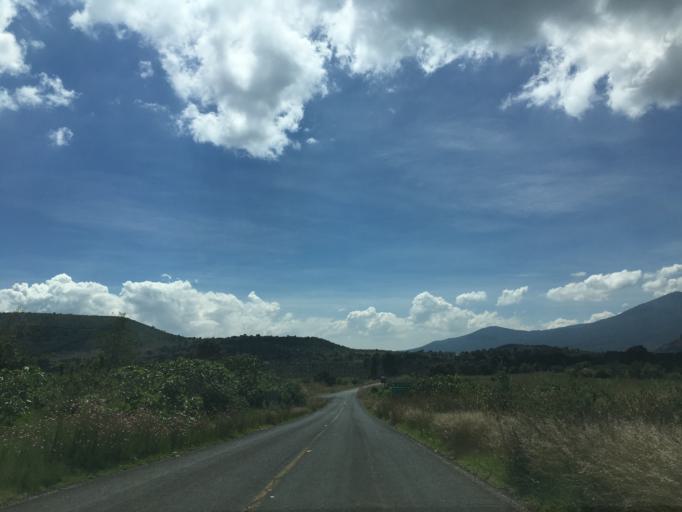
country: MX
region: Michoacan
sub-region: Morelia
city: Cuto de la Esperanza
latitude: 19.7203
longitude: -101.3420
